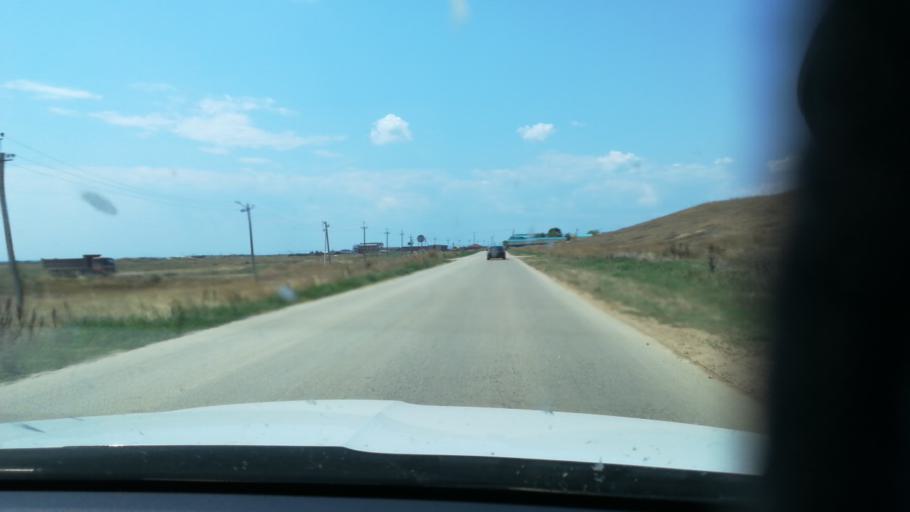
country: RU
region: Krasnodarskiy
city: Vyshestebliyevskaya
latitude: 45.1152
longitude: 36.8905
